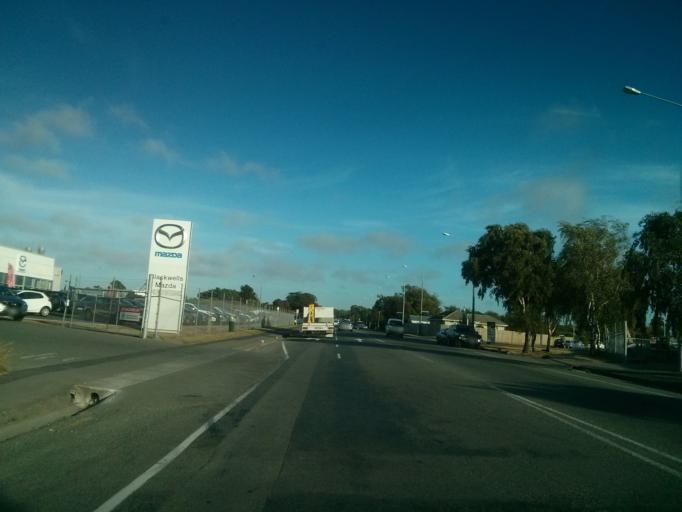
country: NZ
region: Canterbury
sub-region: Selwyn District
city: Prebbleton
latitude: -43.5380
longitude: 172.5483
